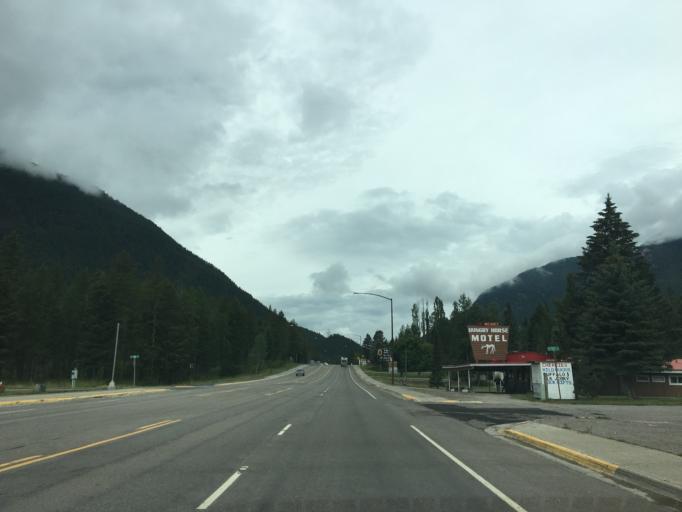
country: US
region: Montana
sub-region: Flathead County
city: Columbia Falls
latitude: 48.3857
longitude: -114.0649
